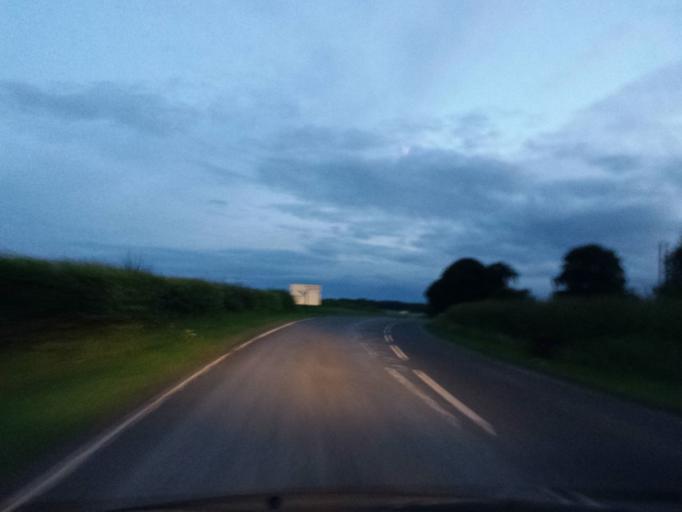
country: GB
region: Scotland
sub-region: The Scottish Borders
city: Duns
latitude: 55.7543
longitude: -2.4028
